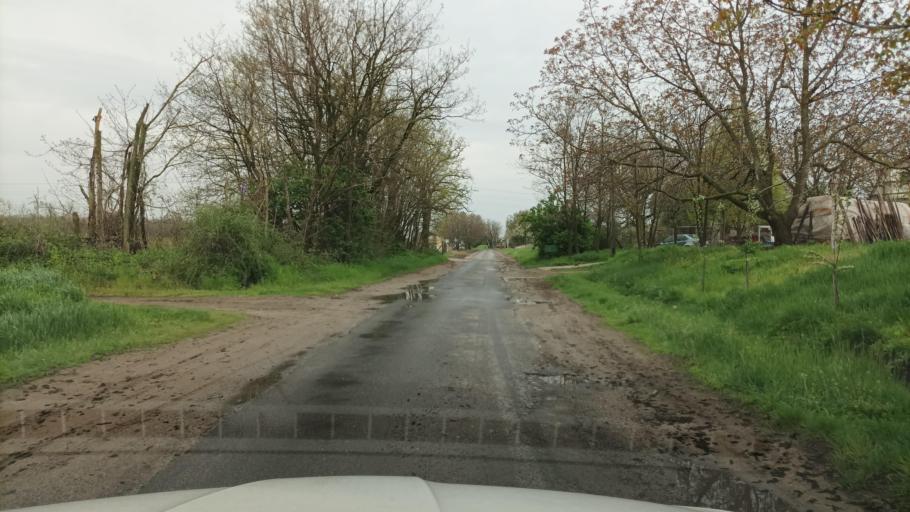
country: HU
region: Pest
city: Nagykoros
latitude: 47.0094
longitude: 19.7962
